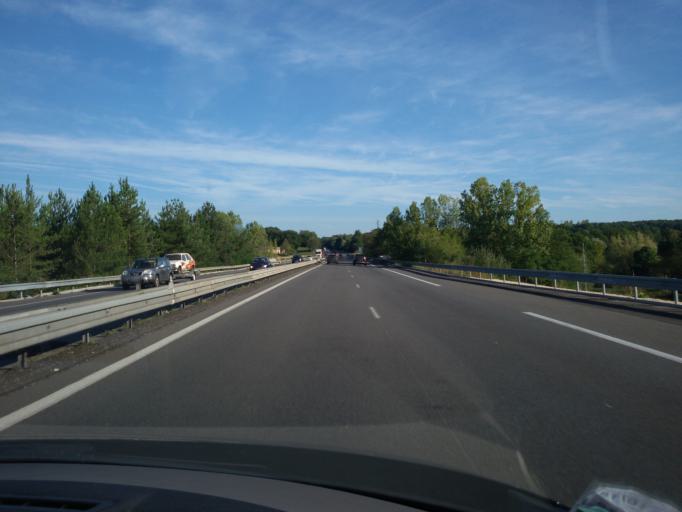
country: FR
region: Centre
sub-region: Departement du Cher
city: Vierzon
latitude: 47.2139
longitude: 2.1143
